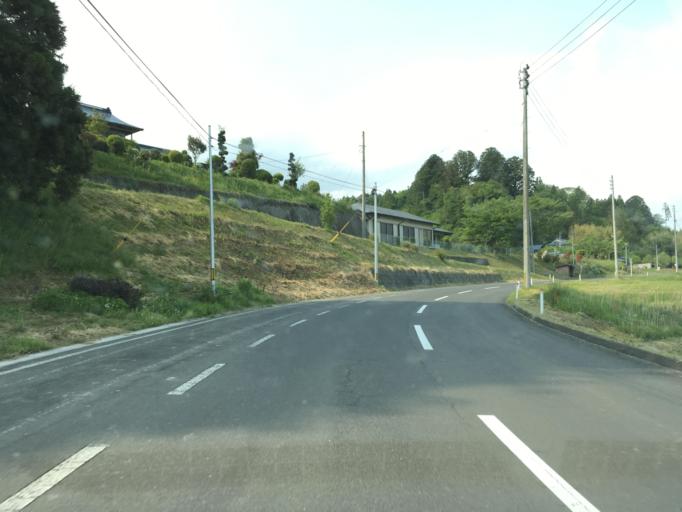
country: JP
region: Iwate
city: Ichinoseki
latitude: 38.9512
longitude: 141.3502
